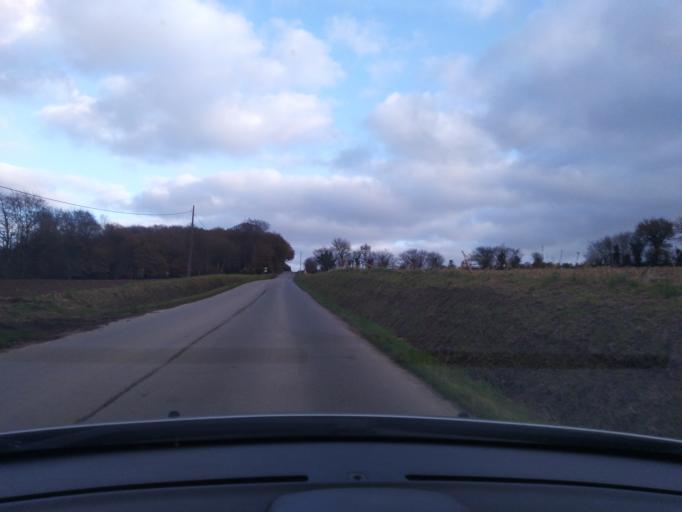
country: FR
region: Brittany
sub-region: Departement du Finistere
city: Plouigneau
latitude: 48.5673
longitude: -3.6723
